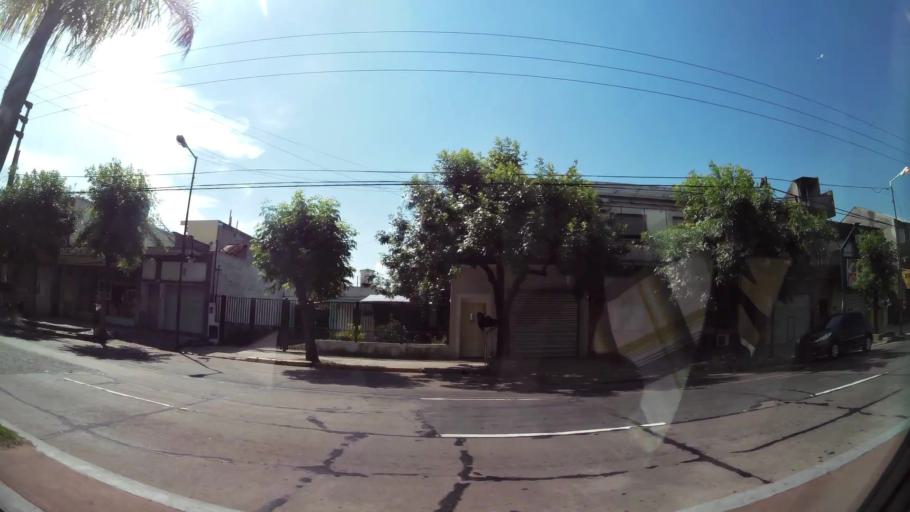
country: AR
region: Buenos Aires
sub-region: Partido de Tigre
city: Tigre
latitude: -34.4671
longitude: -58.5862
